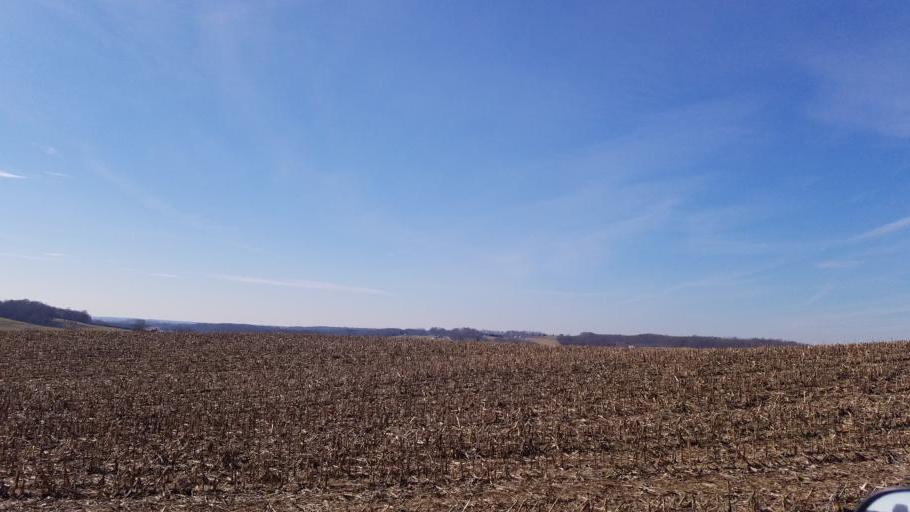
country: US
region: Ohio
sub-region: Knox County
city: Fredericktown
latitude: 40.5209
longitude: -82.4582
